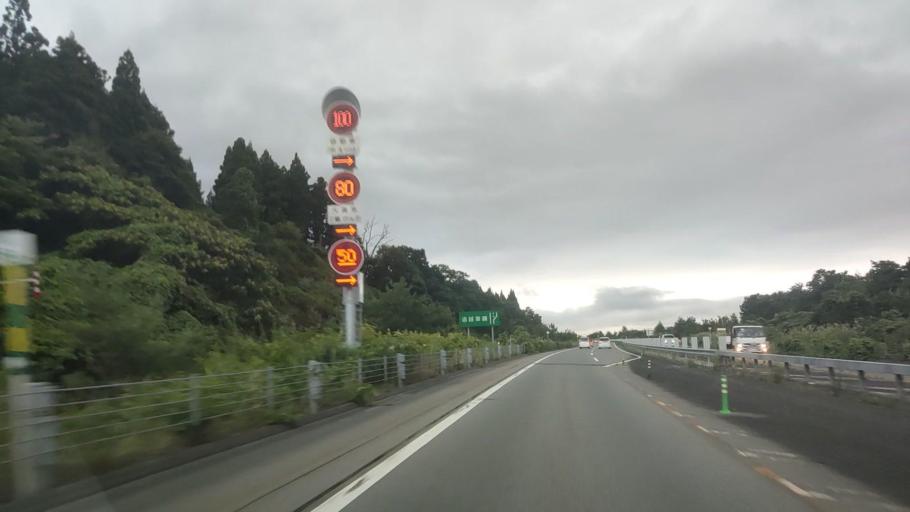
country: JP
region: Hokkaido
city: Nanae
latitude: 41.9074
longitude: 140.6964
